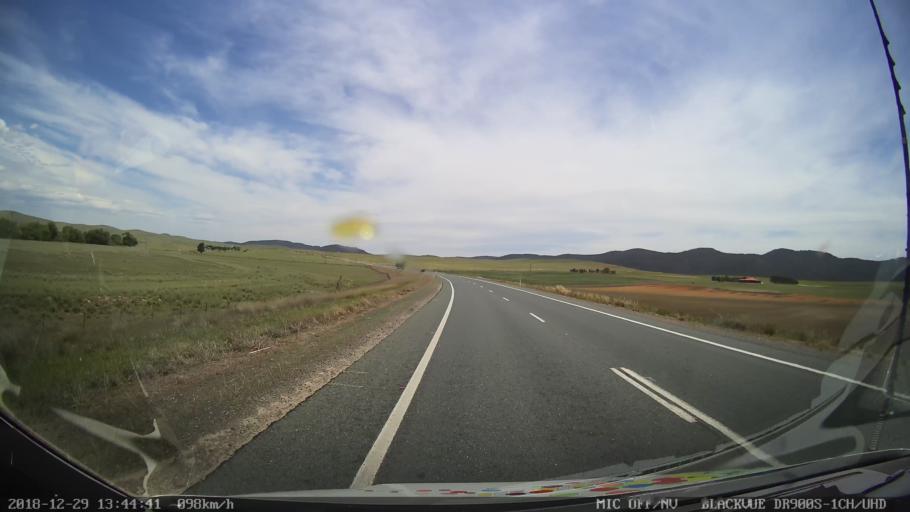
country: AU
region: New South Wales
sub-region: Cooma-Monaro
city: Cooma
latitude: -36.0857
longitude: 149.1485
